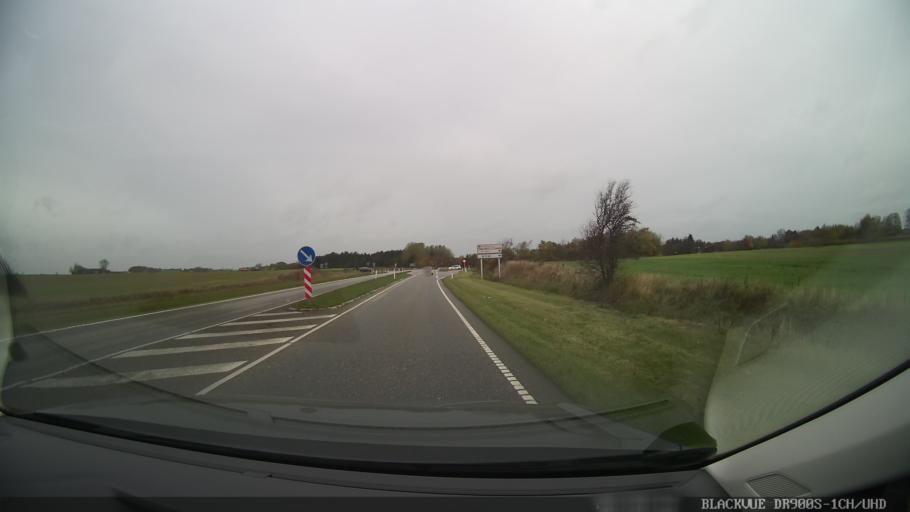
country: DK
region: North Denmark
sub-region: Thisted Kommune
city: Thisted
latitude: 56.8293
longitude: 8.7148
